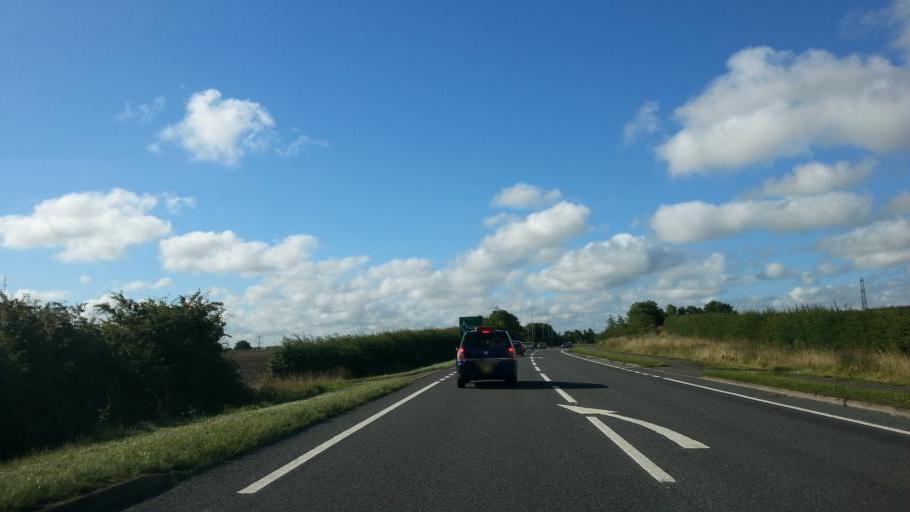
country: GB
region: England
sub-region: Northamptonshire
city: Broughton
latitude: 52.3702
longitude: -0.7843
